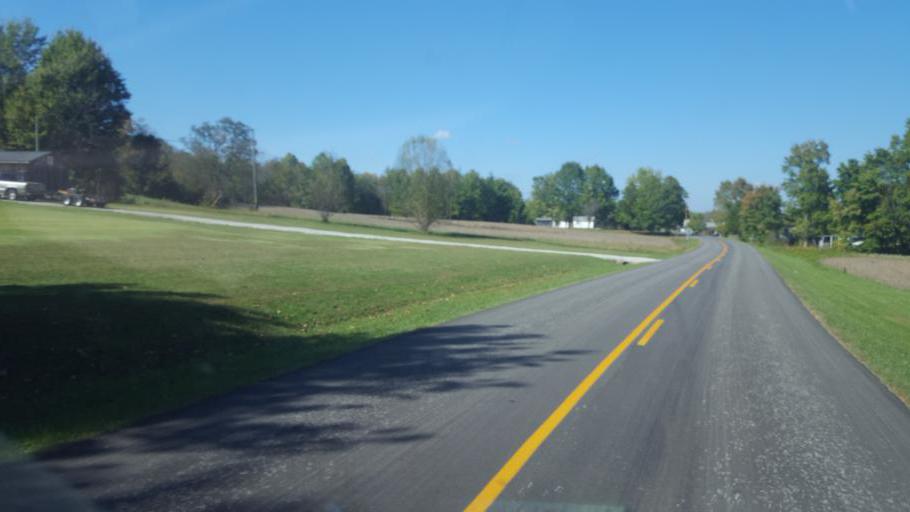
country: US
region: Kentucky
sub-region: Fleming County
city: Flemingsburg
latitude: 38.4644
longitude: -83.5871
